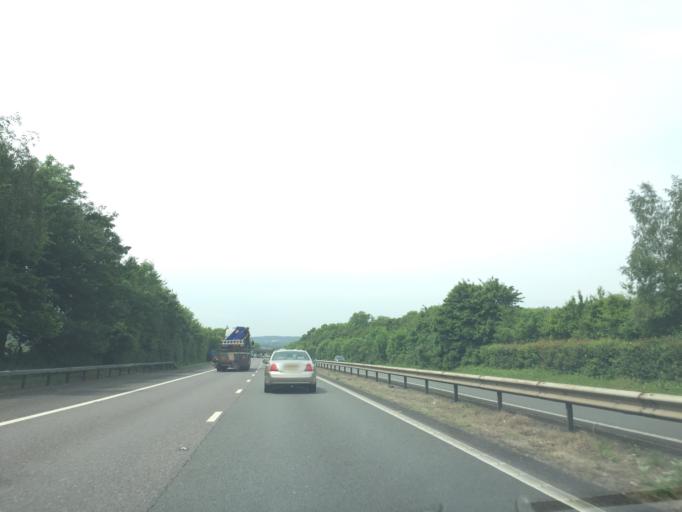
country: GB
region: England
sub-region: Kent
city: Kemsing
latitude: 51.3012
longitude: 0.2396
